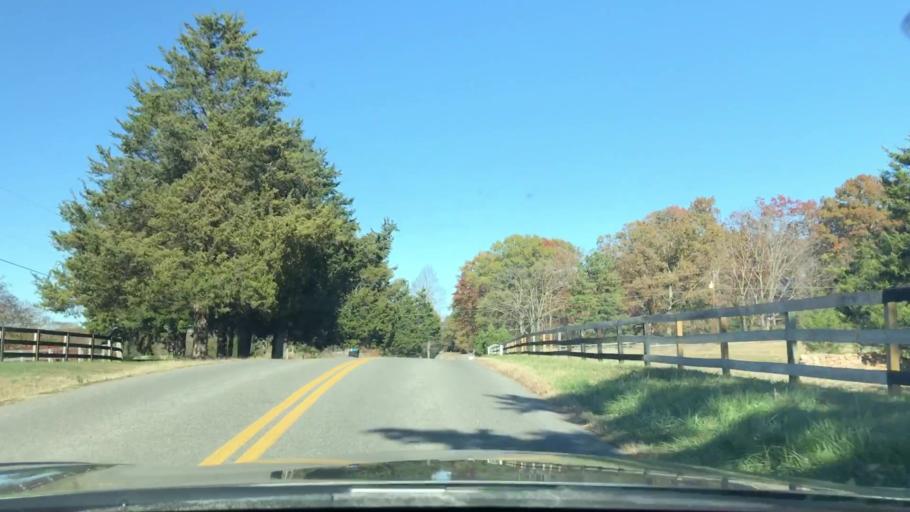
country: US
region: Virginia
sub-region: Henrico County
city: Short Pump
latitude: 37.6605
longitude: -77.7153
